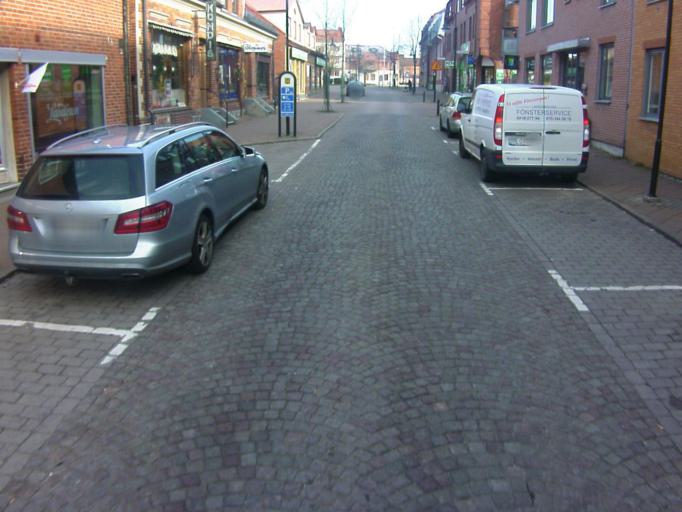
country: SE
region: Skane
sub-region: Kavlinge Kommun
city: Kaevlinge
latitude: 55.7919
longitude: 13.1103
